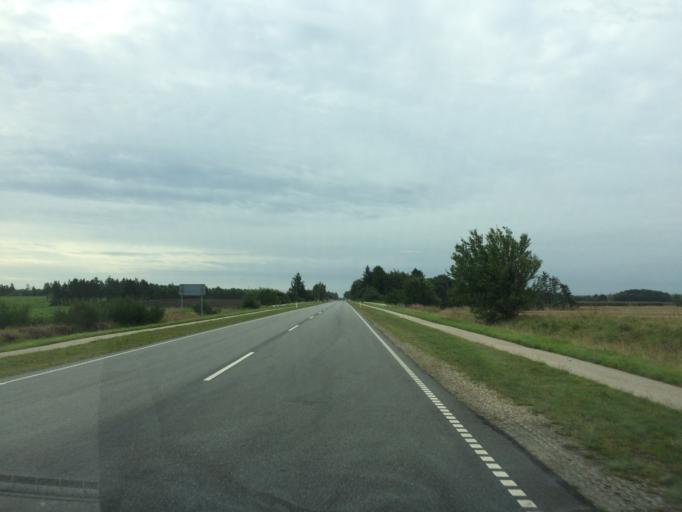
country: DK
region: Central Jutland
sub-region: Herning Kommune
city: Lind
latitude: 56.0756
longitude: 8.9861
